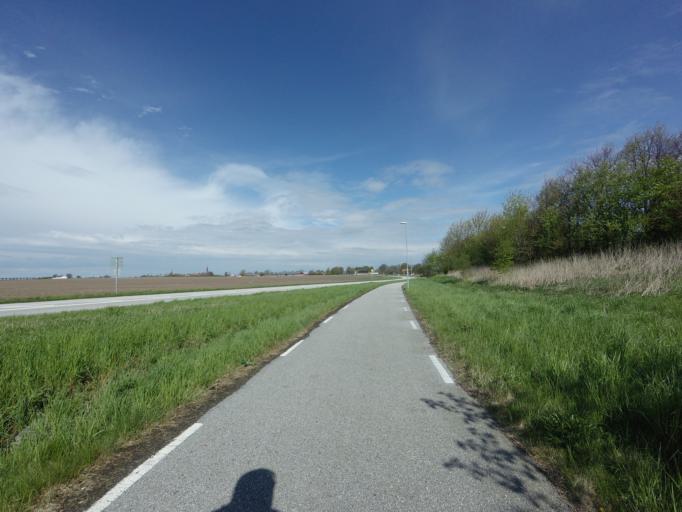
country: SE
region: Skane
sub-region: Malmo
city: Tygelsjo
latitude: 55.4960
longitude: 13.0008
